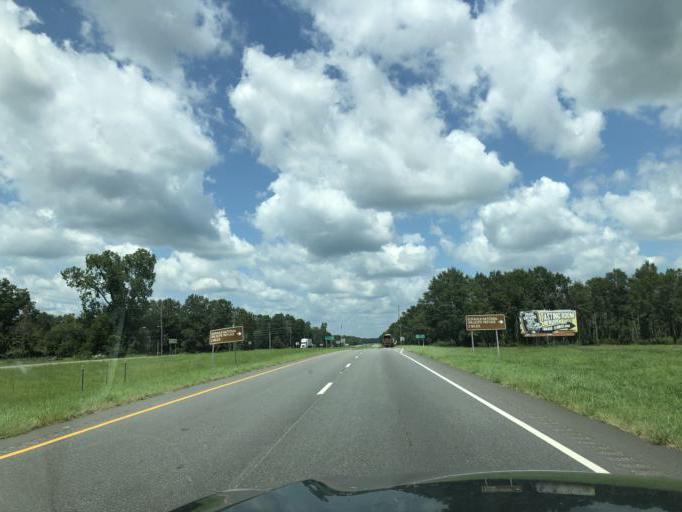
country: US
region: Alabama
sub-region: Barbour County
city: Eufaula
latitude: 31.9985
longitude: -85.1155
